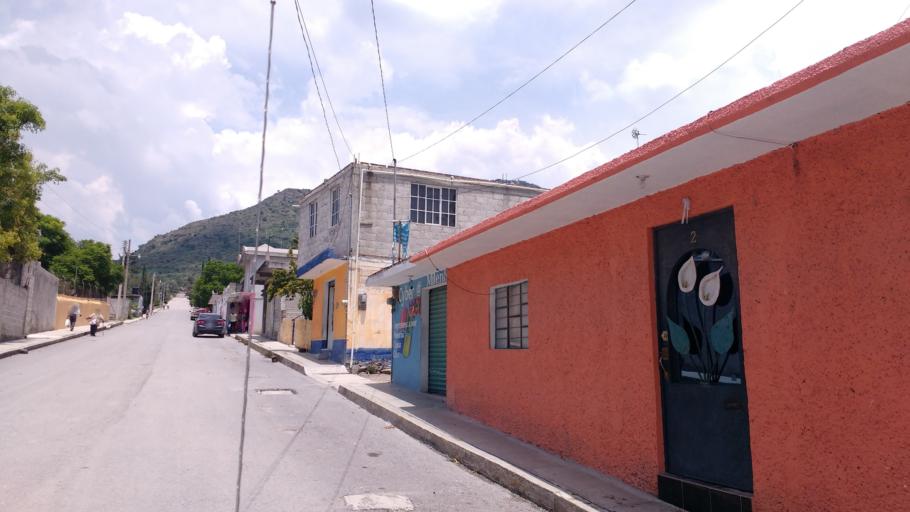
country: MX
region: Hidalgo
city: Mixquiahuala de Juarez
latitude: 20.2507
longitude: -99.2442
